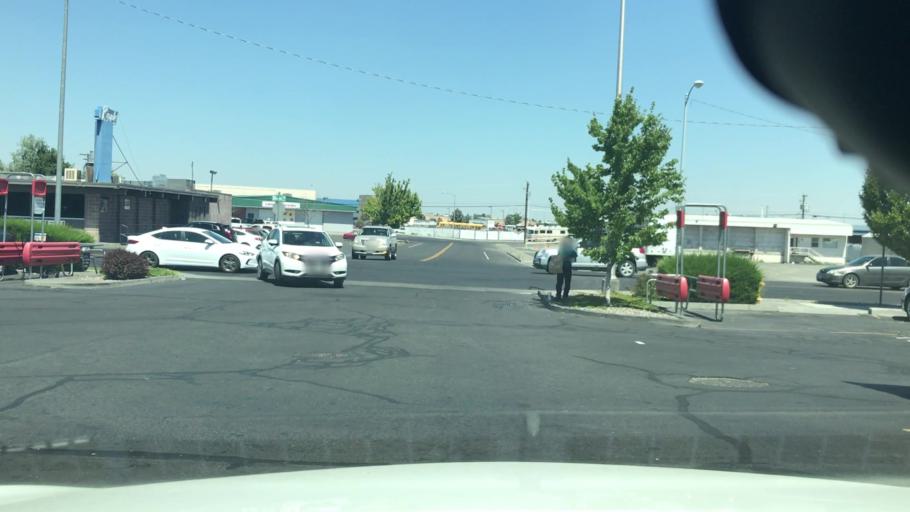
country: US
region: Washington
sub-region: Grant County
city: Moses Lake
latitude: 47.1308
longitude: -119.2687
